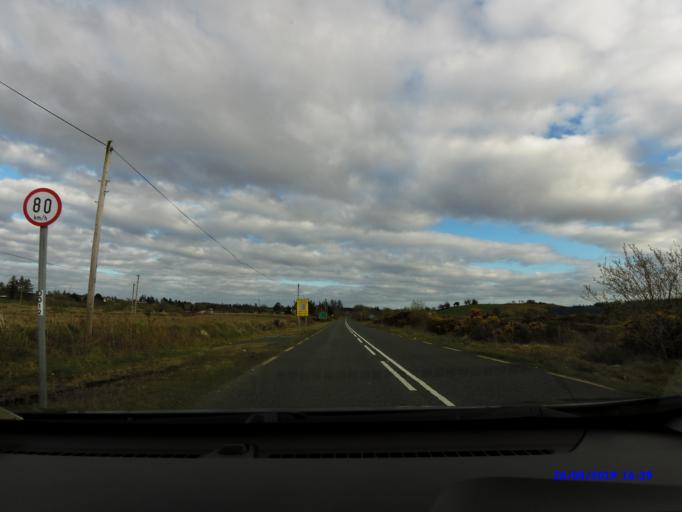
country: IE
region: Connaught
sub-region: Maigh Eo
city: Ballyhaunis
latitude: 53.8858
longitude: -8.8004
